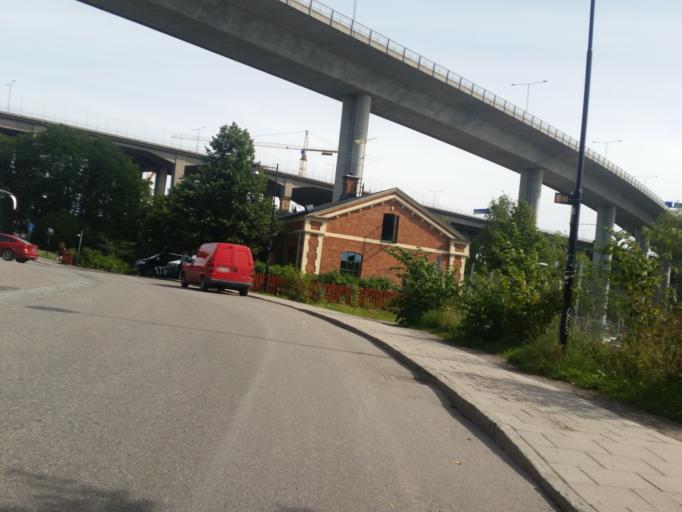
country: SE
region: Stockholm
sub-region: Stockholms Kommun
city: Arsta
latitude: 59.3037
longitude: 18.0760
